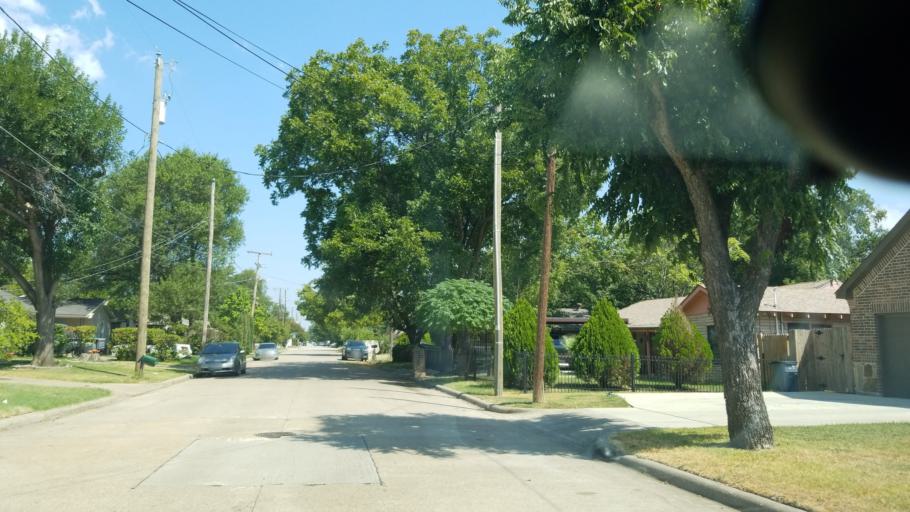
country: US
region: Texas
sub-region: Dallas County
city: Grand Prairie
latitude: 32.7091
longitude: -96.9845
